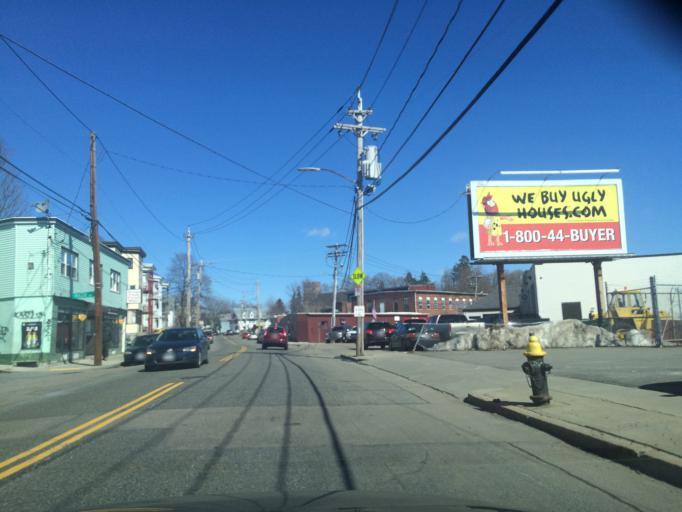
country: US
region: Massachusetts
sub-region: Norfolk County
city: Dedham
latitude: 42.2500
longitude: -71.1309
